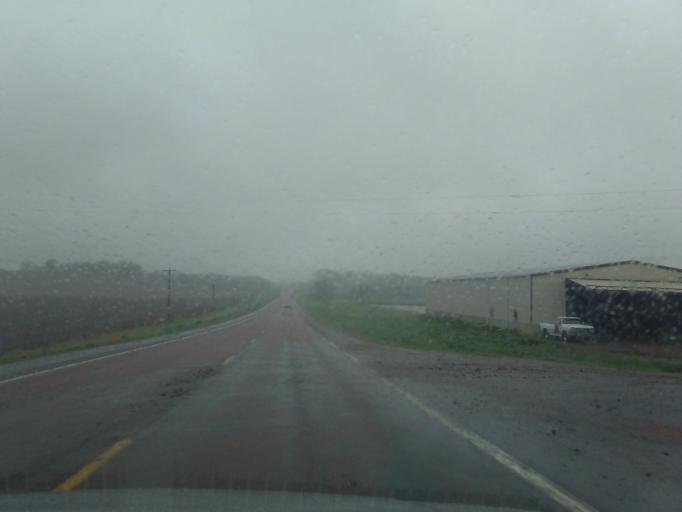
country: US
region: Nebraska
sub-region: Wayne County
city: Wayne
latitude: 42.2354
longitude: -97.1651
